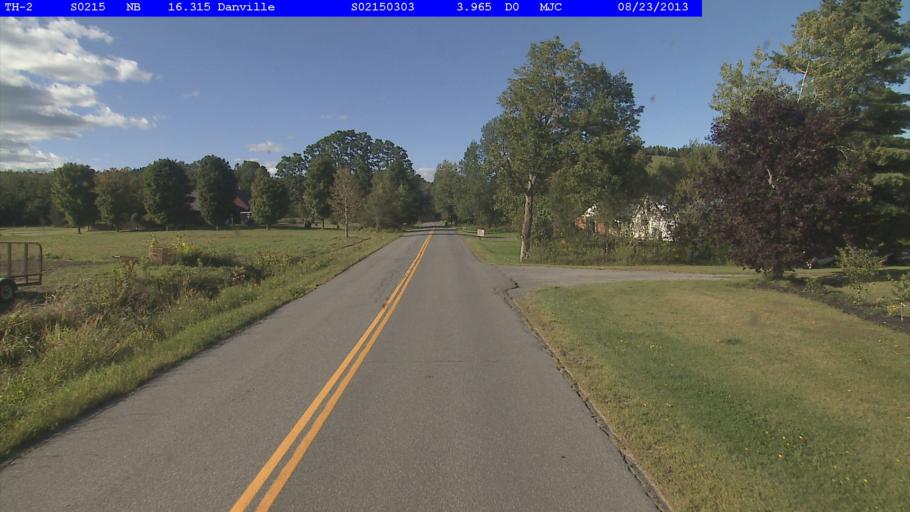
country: US
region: Vermont
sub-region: Caledonia County
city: Saint Johnsbury
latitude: 44.4211
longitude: -72.1421
